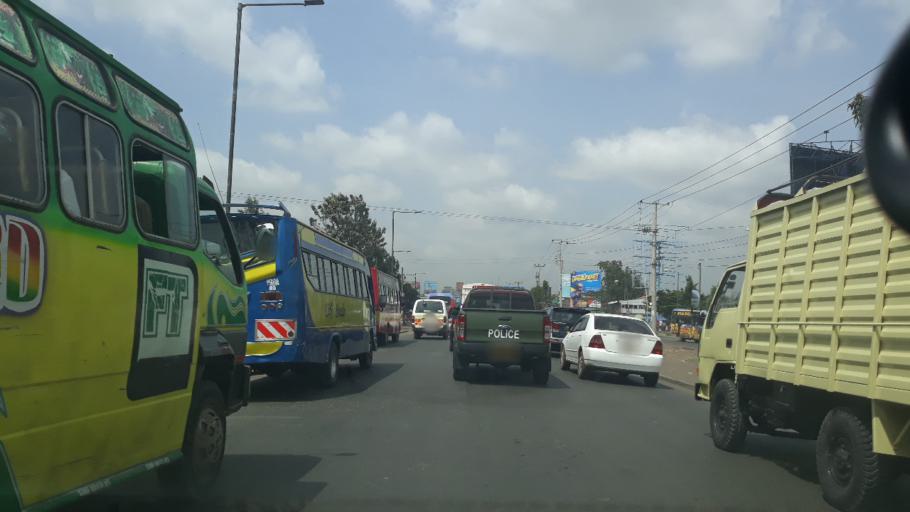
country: KE
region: Nairobi Area
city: Pumwani
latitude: -1.2931
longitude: 36.8459
